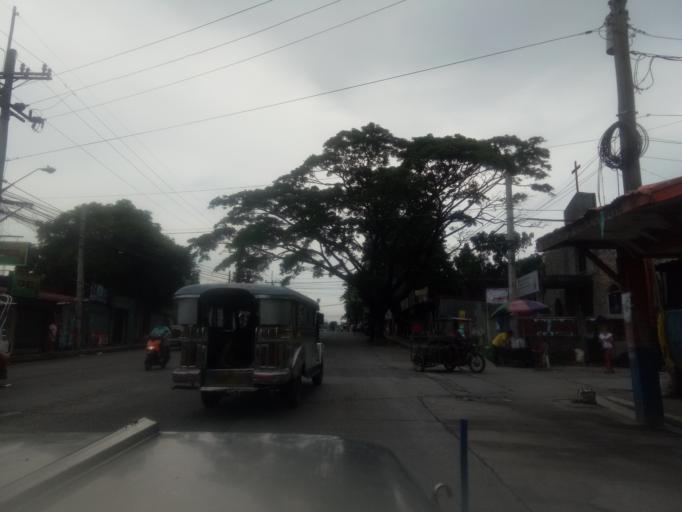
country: PH
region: Calabarzon
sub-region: Province of Cavite
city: Bulihan
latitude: 14.2966
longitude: 121.0078
